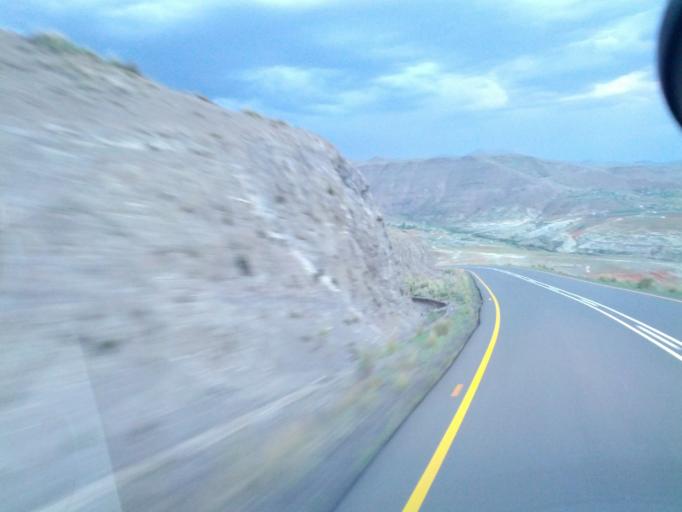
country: LS
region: Qacha's Nek
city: Qacha's Nek
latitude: -30.0444
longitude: 28.3091
